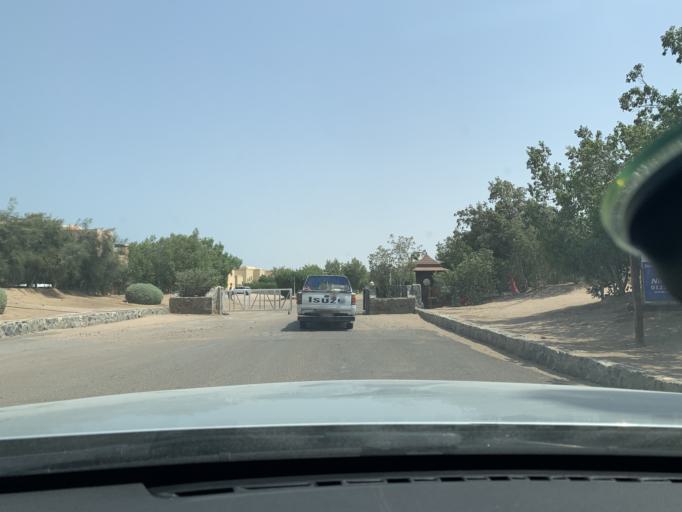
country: EG
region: Red Sea
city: El Gouna
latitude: 27.3903
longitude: 33.6691
